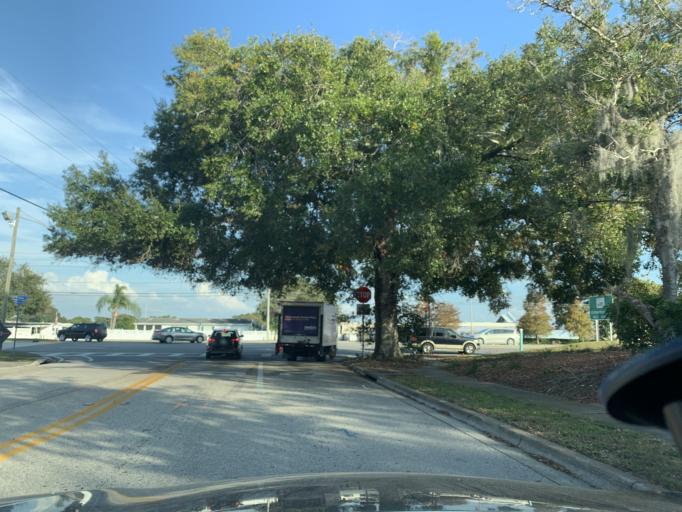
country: US
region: Florida
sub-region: Pinellas County
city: Ridgecrest
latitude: 27.8966
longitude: -82.7959
